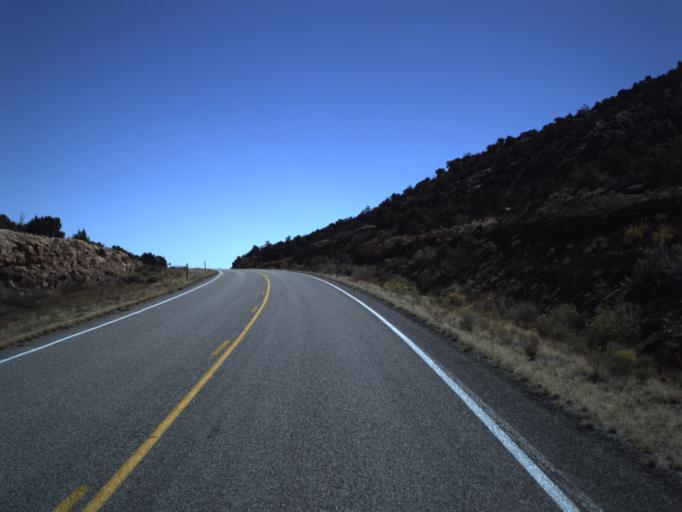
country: US
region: Utah
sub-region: San Juan County
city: Blanding
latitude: 37.5988
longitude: -110.0537
